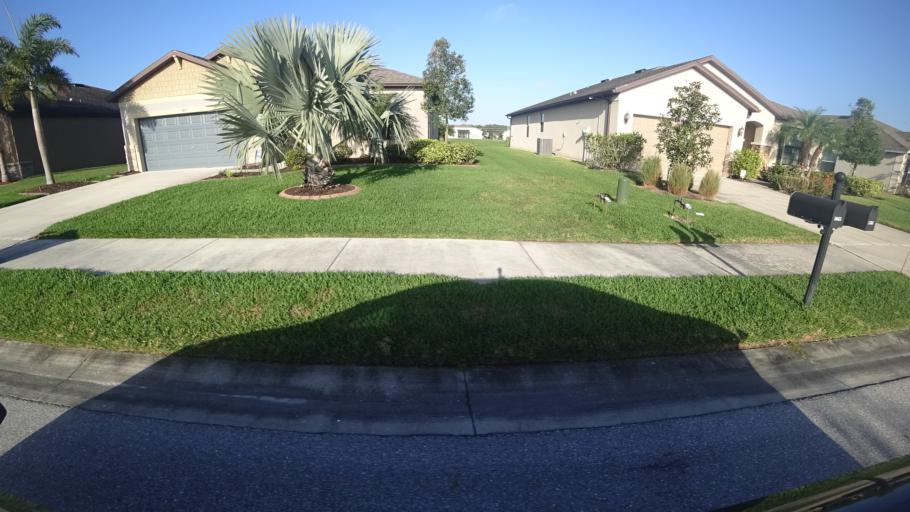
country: US
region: Florida
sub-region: Manatee County
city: Ellenton
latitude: 27.5677
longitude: -82.4542
